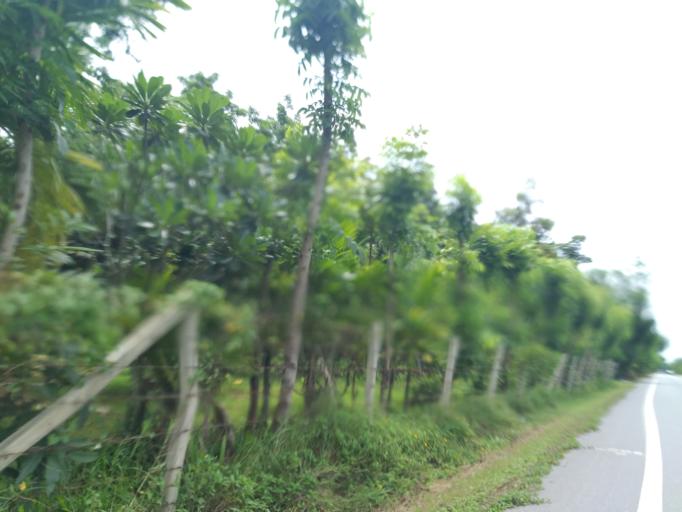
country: TH
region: Pathum Thani
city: Nong Suea
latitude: 14.0610
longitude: 100.8715
